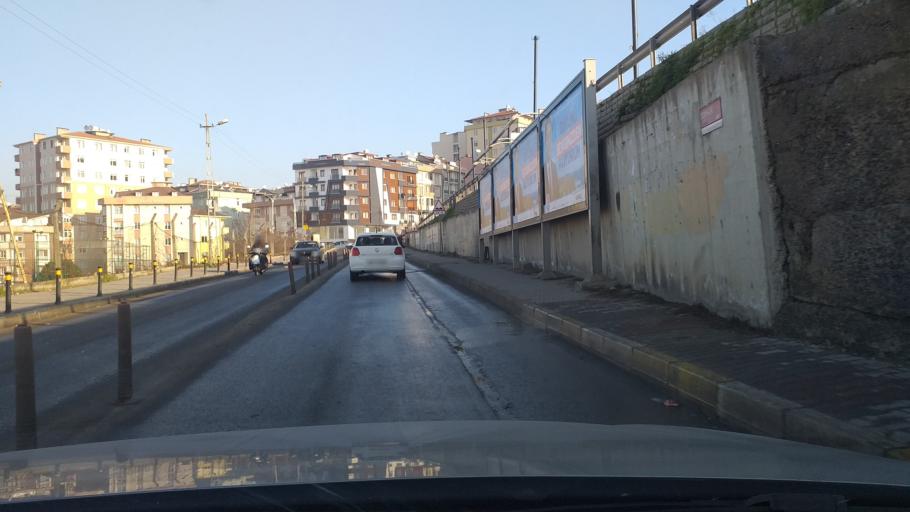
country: TR
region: Istanbul
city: Maltepe
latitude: 40.9338
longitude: 29.1527
